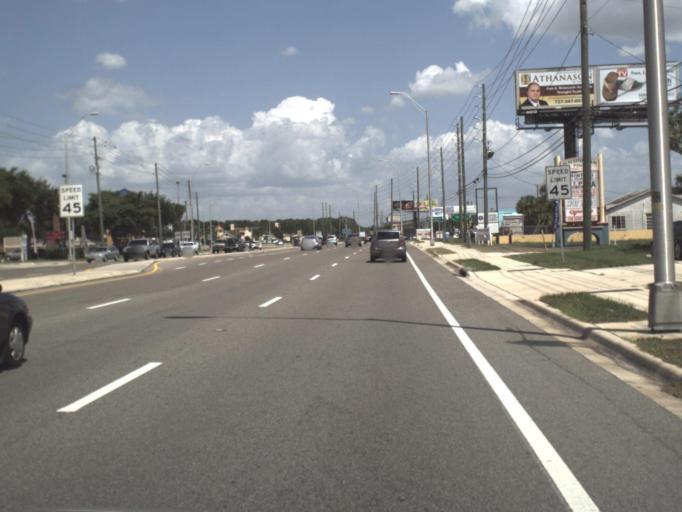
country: US
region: Florida
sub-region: Pinellas County
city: Ridgecrest
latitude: 27.8802
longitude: -82.8192
